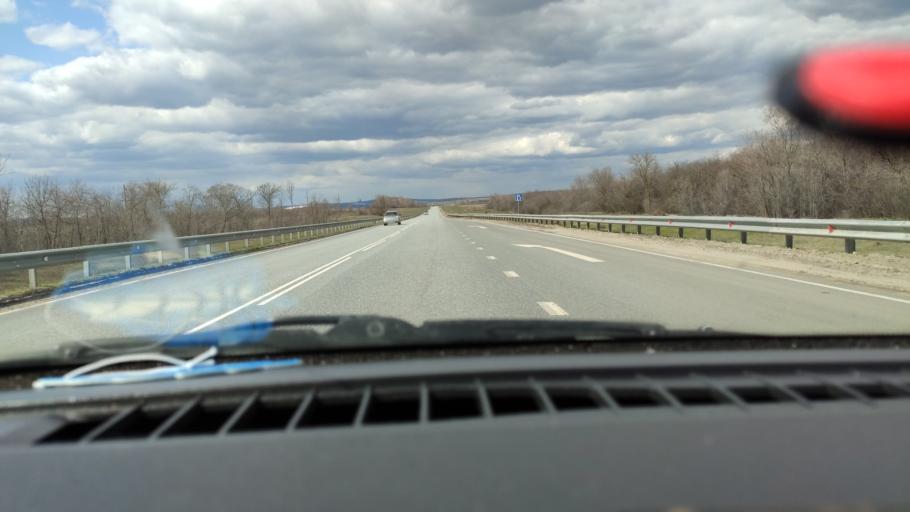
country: RU
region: Saratov
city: Tersa
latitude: 52.0844
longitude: 47.6423
